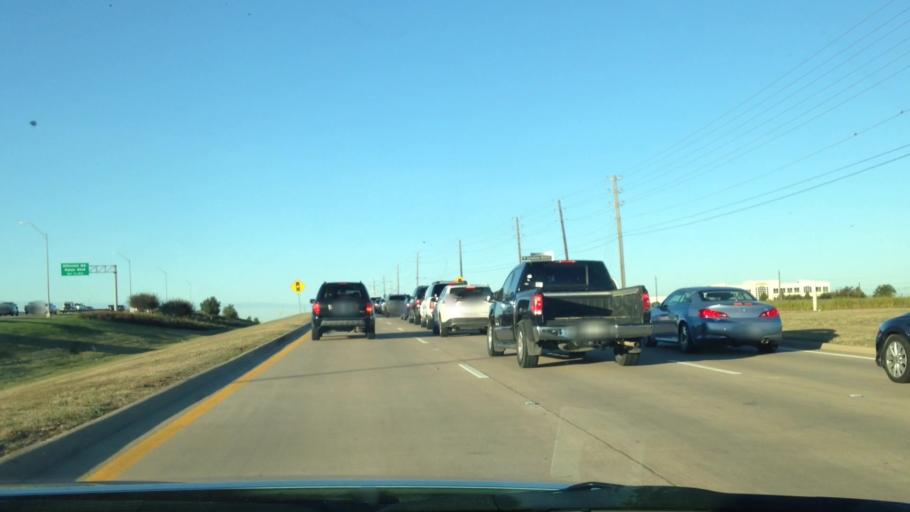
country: US
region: Texas
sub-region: Collin County
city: Frisco
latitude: 33.1144
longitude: -96.7644
